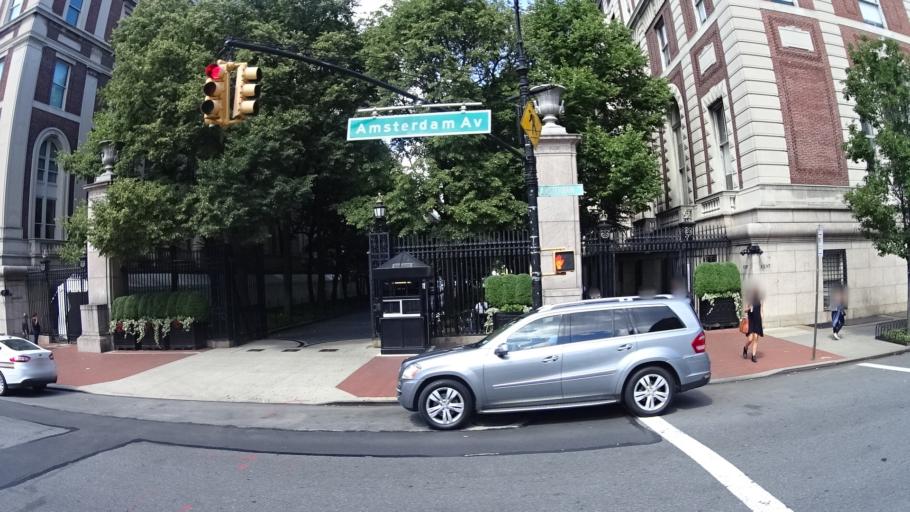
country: US
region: New York
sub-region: New York County
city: Manhattan
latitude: 40.8068
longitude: -73.9611
